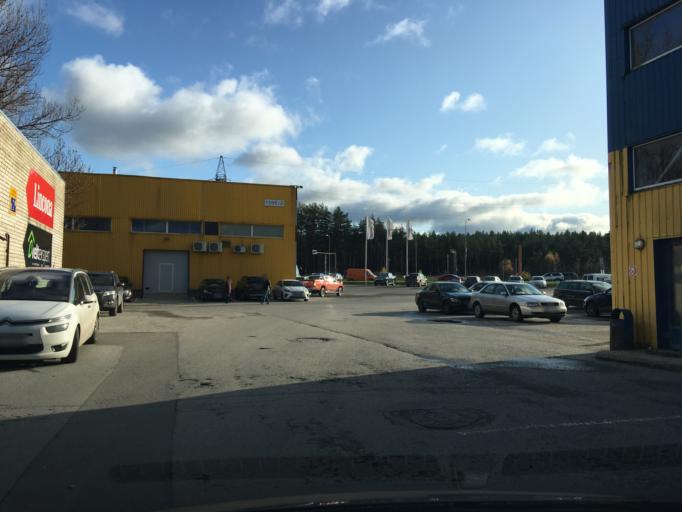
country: EE
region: Harju
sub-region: Tallinna linn
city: Tallinn
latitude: 59.4048
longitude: 24.7349
